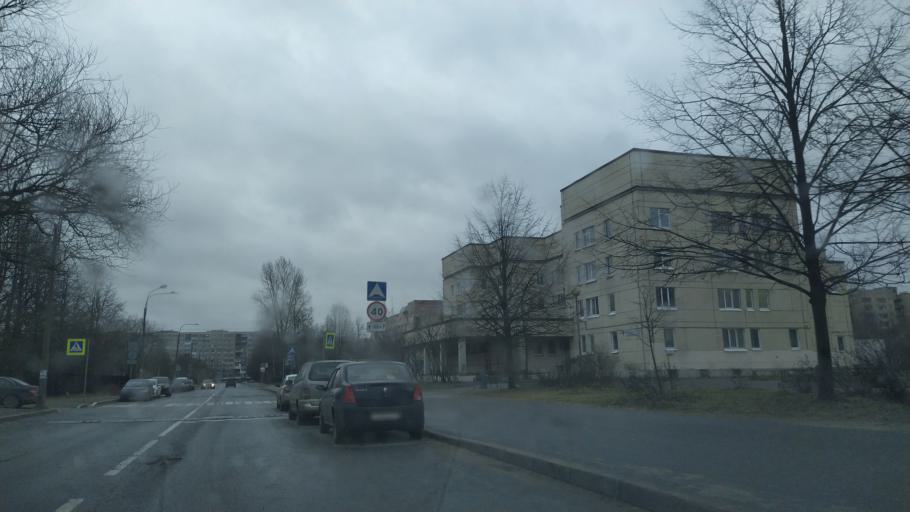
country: RU
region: Leningrad
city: Akademicheskoe
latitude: 60.0244
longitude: 30.3872
